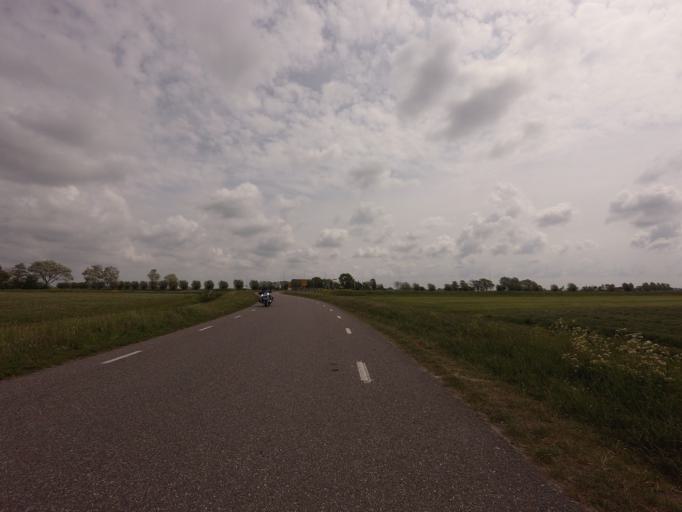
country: NL
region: Friesland
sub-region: Sudwest Fryslan
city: Bolsward
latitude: 53.0941
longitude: 5.5320
